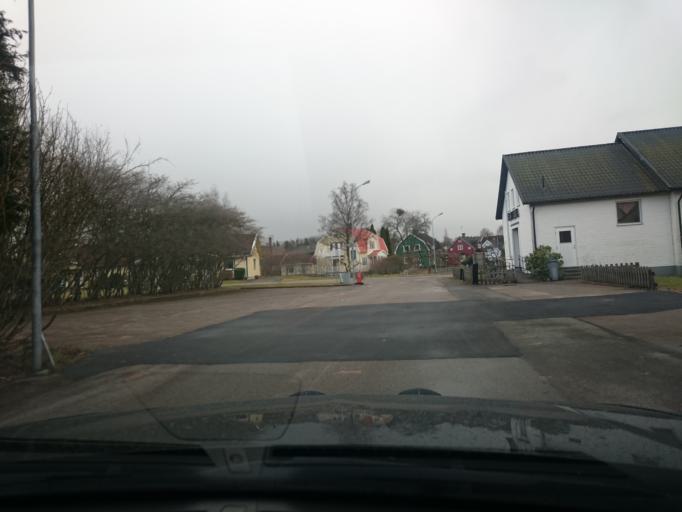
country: SE
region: Joenkoeping
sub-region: Vetlanda Kommun
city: Vetlanda
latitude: 57.3031
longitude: 15.1236
